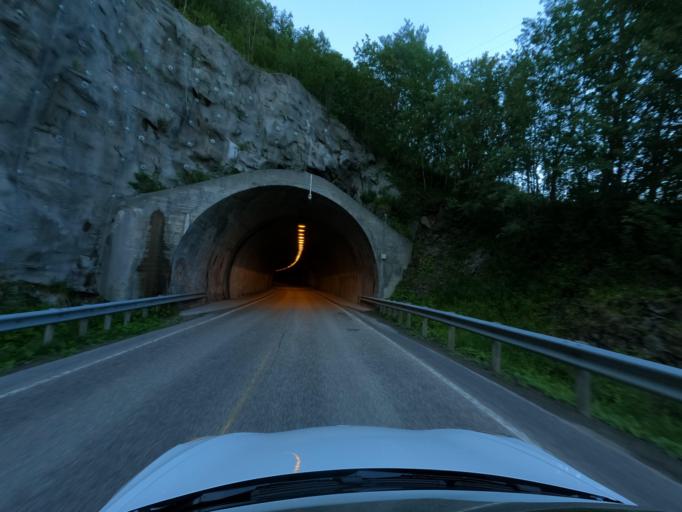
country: NO
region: Troms
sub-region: Harstad
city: Harstad
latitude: 68.7306
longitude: 16.5480
